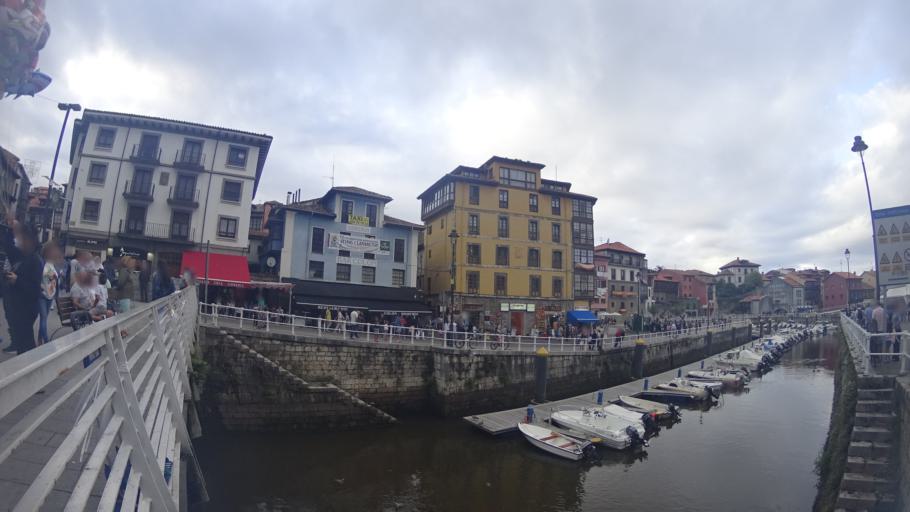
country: ES
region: Asturias
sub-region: Province of Asturias
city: Llanes
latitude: 43.4196
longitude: -4.7544
